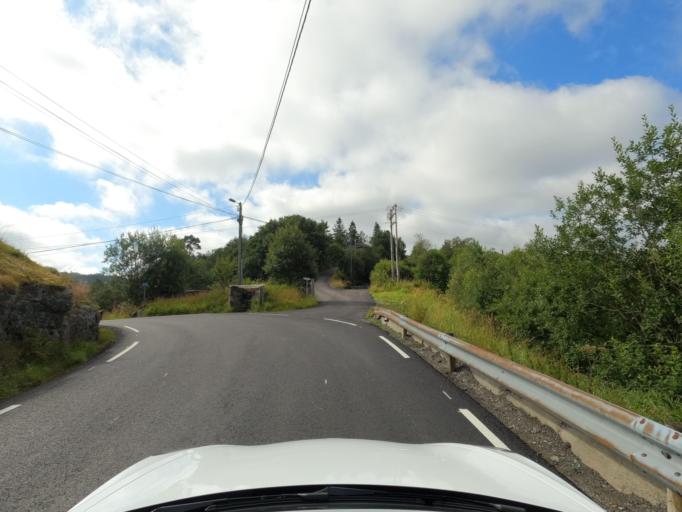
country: NO
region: Hordaland
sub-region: Os
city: Syfteland
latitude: 60.3046
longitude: 5.4179
